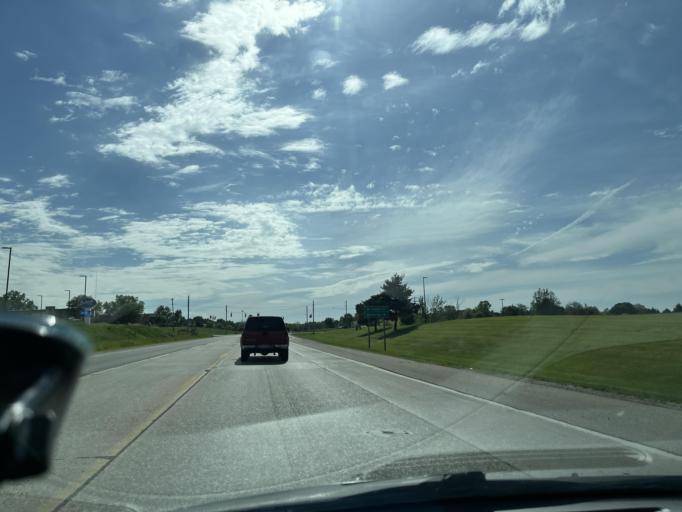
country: US
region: Michigan
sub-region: Barry County
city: Hastings
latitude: 42.6470
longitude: -85.3177
